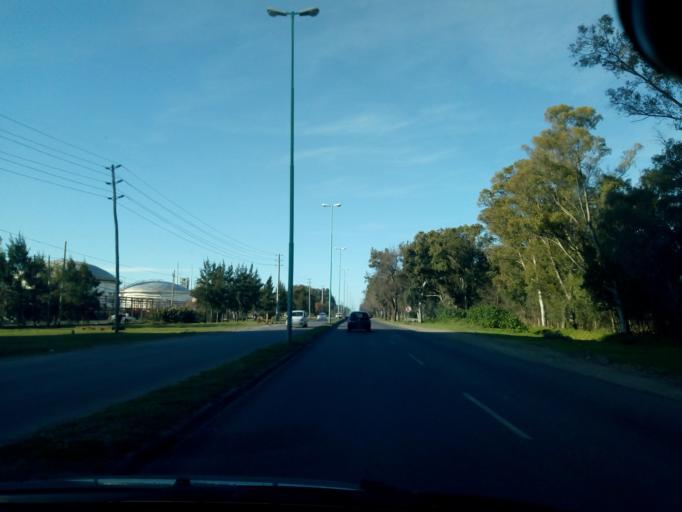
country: AR
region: Buenos Aires
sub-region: Partido de Ensenada
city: Ensenada
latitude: -34.8792
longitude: -57.9218
